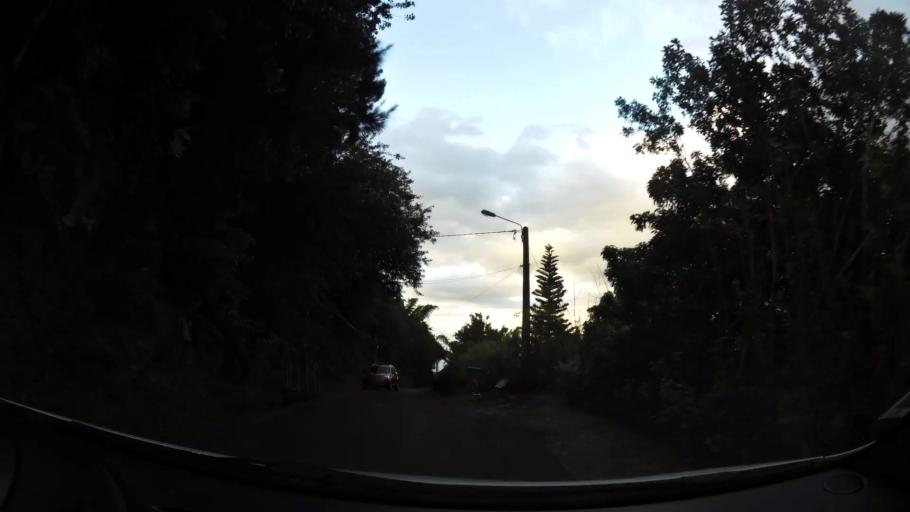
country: RE
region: Reunion
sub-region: Reunion
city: Saint-Denis
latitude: -20.9190
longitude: 55.4631
